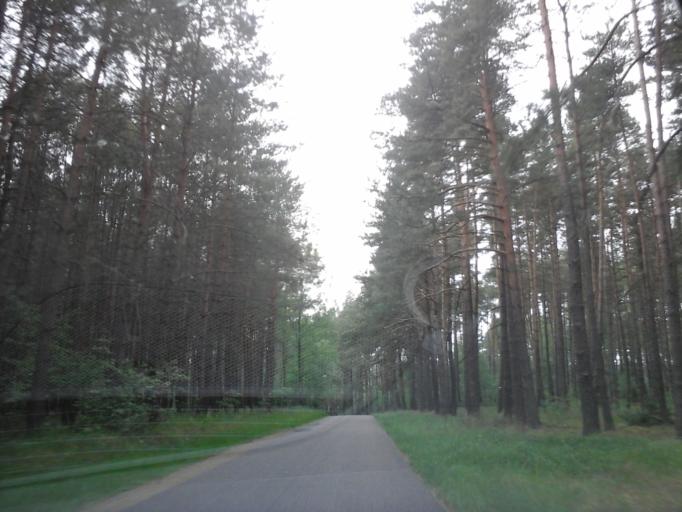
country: PL
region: West Pomeranian Voivodeship
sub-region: Powiat walecki
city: Tuczno
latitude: 53.2311
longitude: 16.0863
